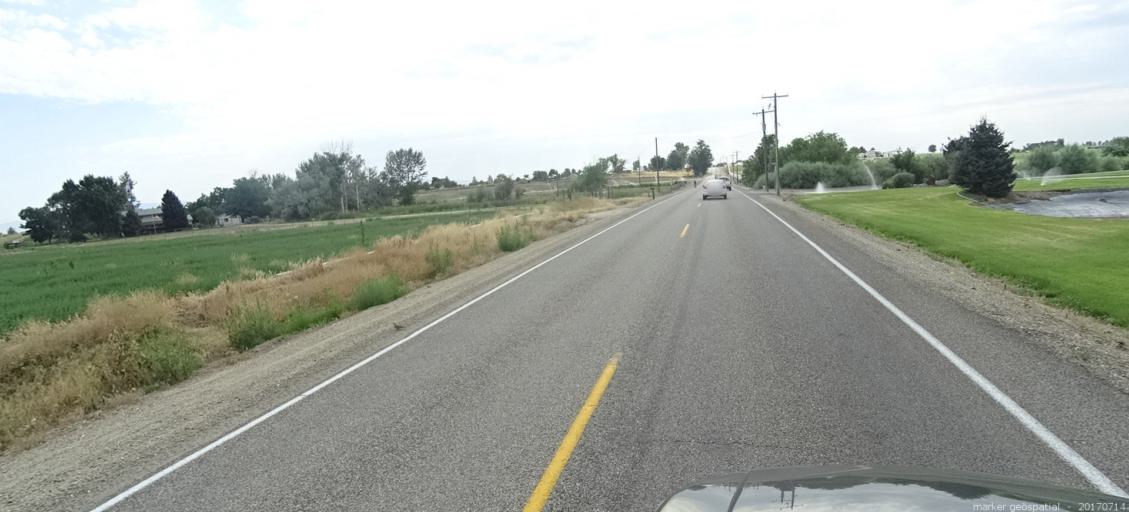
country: US
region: Idaho
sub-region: Ada County
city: Kuna
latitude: 43.4737
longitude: -116.3715
